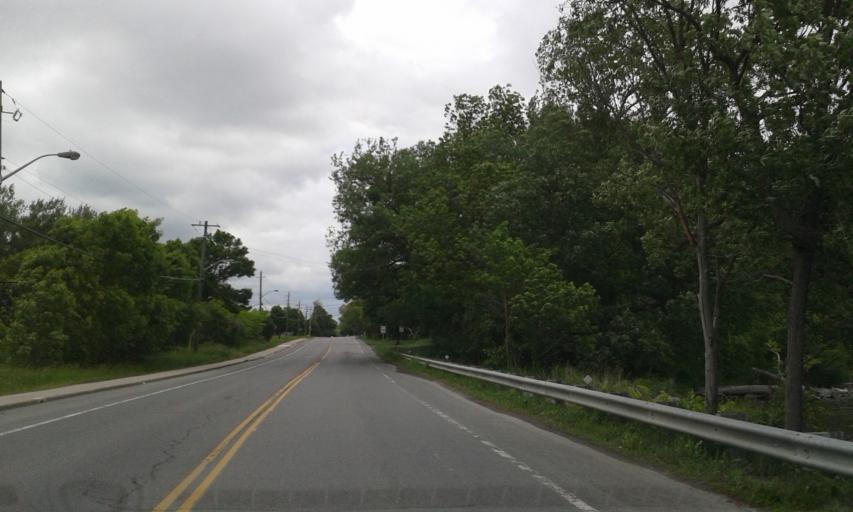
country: CA
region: Ontario
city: Skatepark
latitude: 44.1750
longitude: -76.7872
